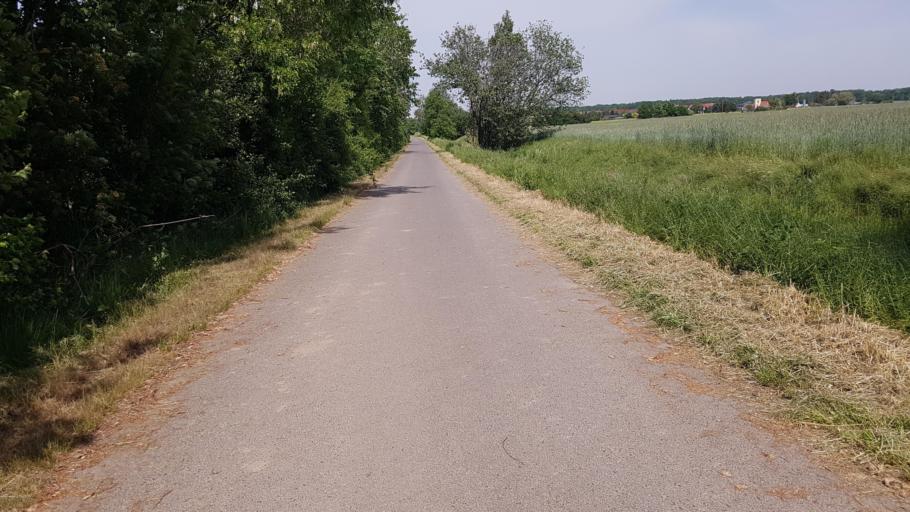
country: DE
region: Brandenburg
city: Grosskmehlen
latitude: 51.3777
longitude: 13.7087
